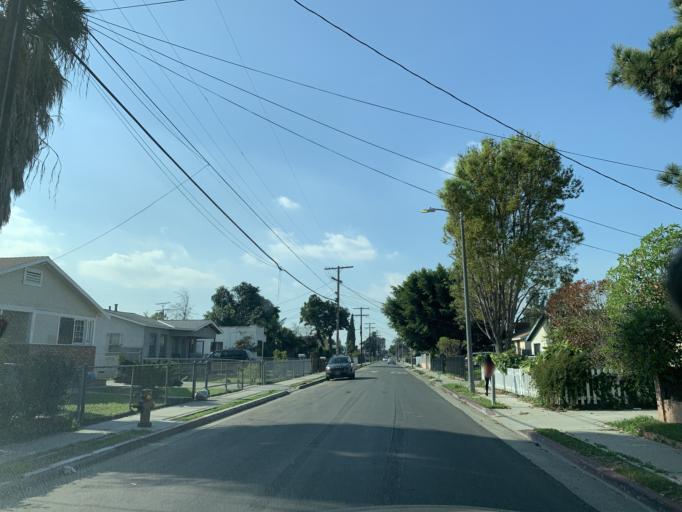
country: US
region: California
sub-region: Los Angeles County
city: Willowbrook
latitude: 33.9304
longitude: -118.2409
